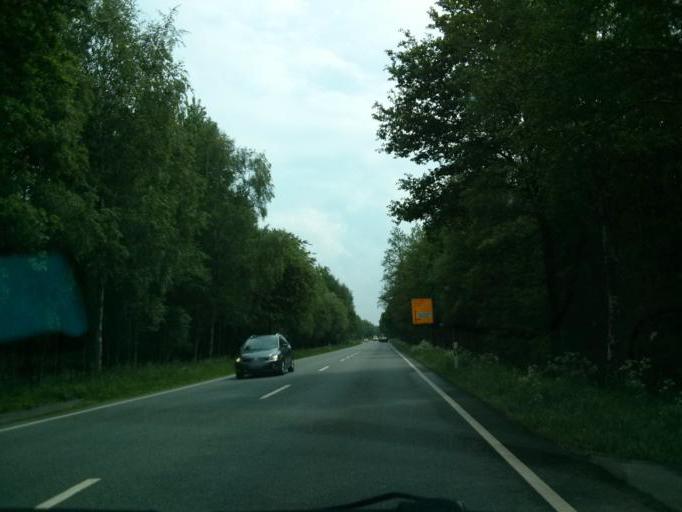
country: DE
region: Lower Saxony
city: Loxstedt
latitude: 53.4879
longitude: 8.6659
